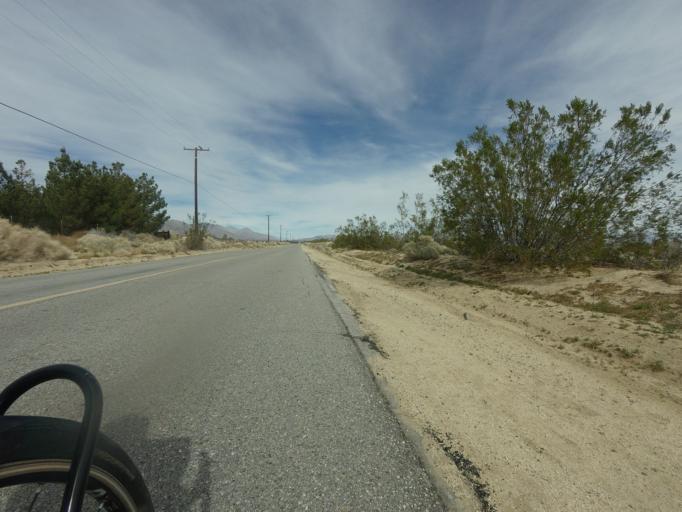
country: US
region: California
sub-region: Kern County
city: Inyokern
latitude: 35.7276
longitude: -117.8362
